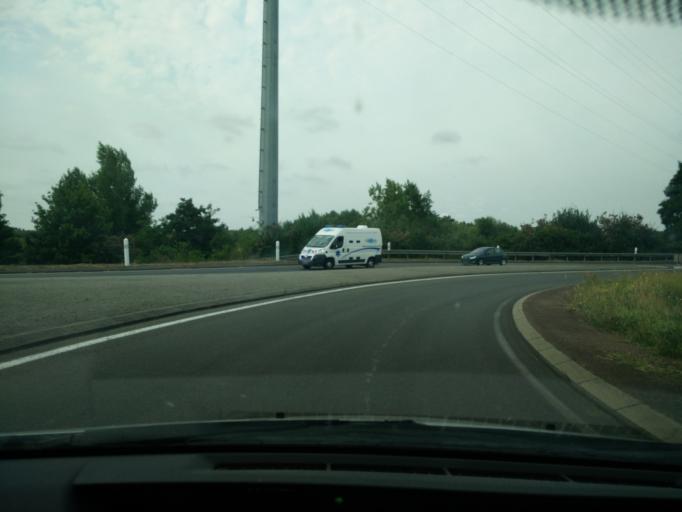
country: FR
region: Pays de la Loire
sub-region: Departement de Maine-et-Loire
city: Doue-la-Fontaine
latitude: 47.1828
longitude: -0.2479
